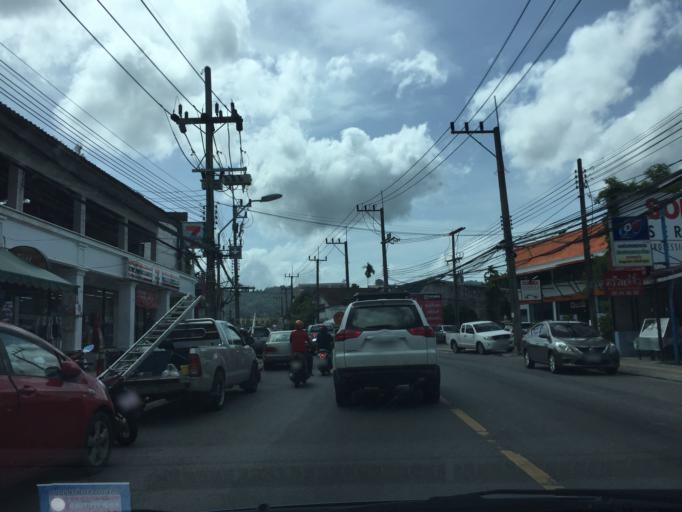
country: TH
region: Phuket
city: Wichit
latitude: 7.8993
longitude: 98.3829
